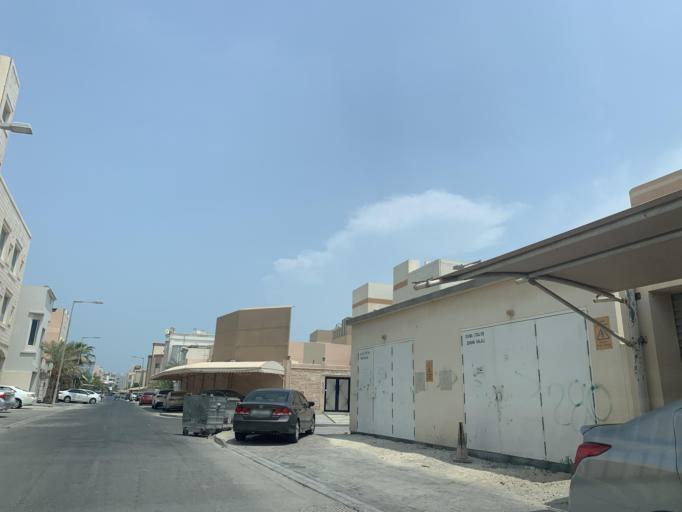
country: BH
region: Muharraq
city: Al Hadd
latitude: 26.2772
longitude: 50.6516
